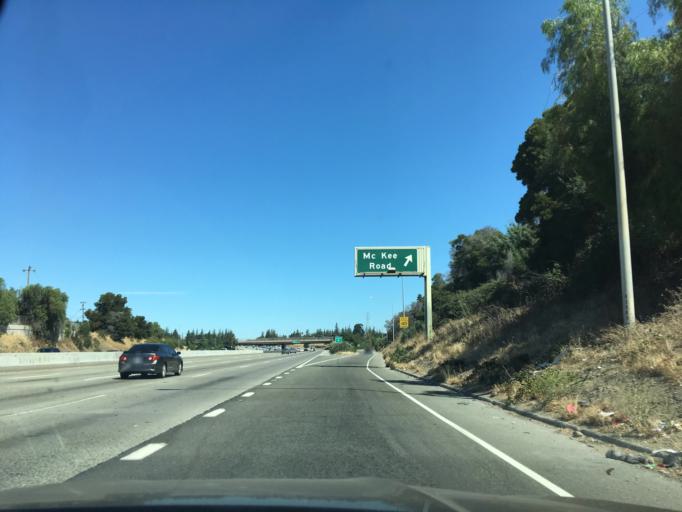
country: US
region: California
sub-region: Santa Clara County
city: Alum Rock
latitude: 37.3642
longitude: -121.8435
